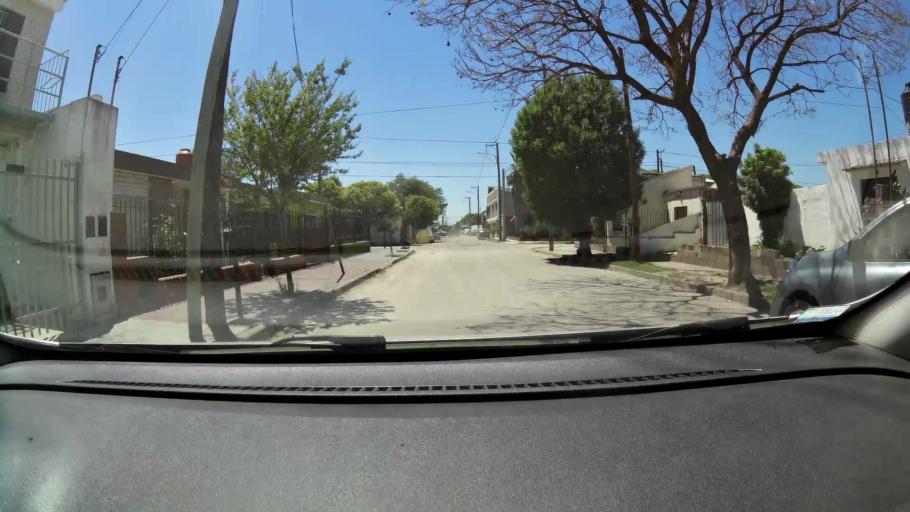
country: AR
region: Cordoba
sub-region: Departamento de Capital
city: Cordoba
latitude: -31.4287
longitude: -64.1256
